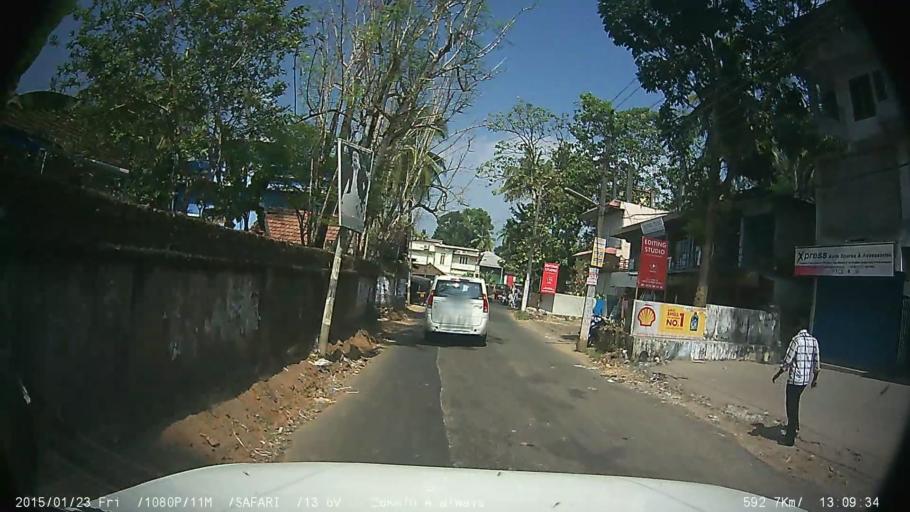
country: IN
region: Kerala
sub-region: Kottayam
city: Changanacheri
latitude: 9.4432
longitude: 76.5455
